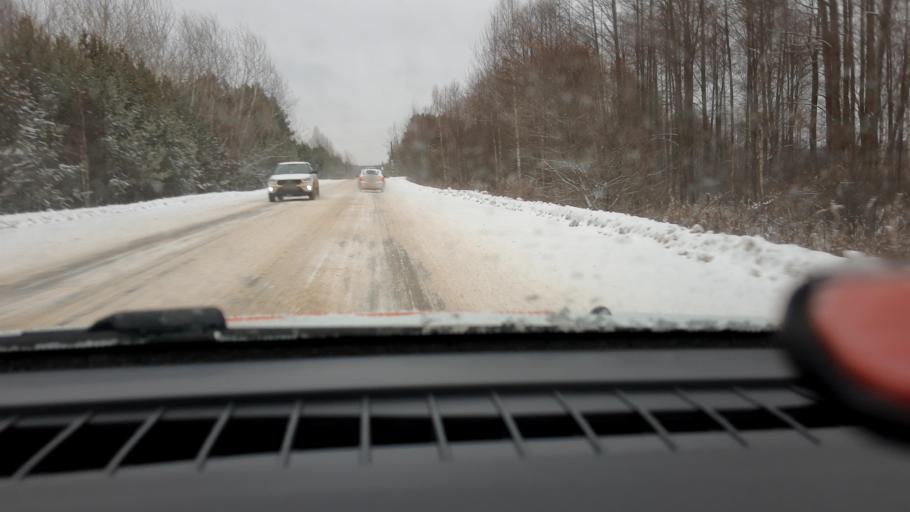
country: RU
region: Nizjnij Novgorod
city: Kstovo
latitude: 56.2779
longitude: 44.3431
